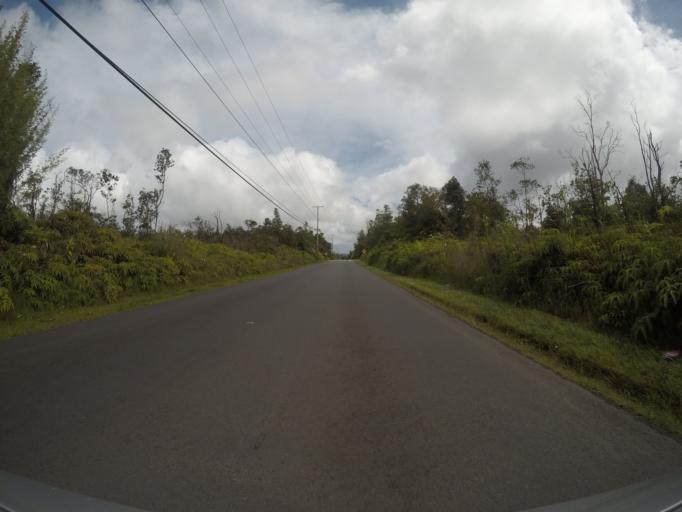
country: US
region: Hawaii
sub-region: Hawaii County
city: Fern Acres
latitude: 19.4747
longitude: -155.1398
